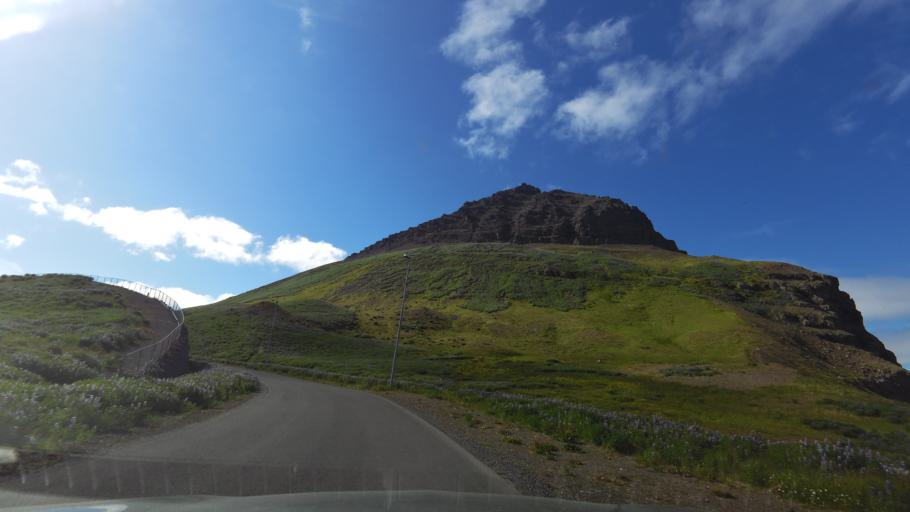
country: IS
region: Westfjords
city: Isafjoerdur
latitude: 66.1625
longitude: -23.2495
